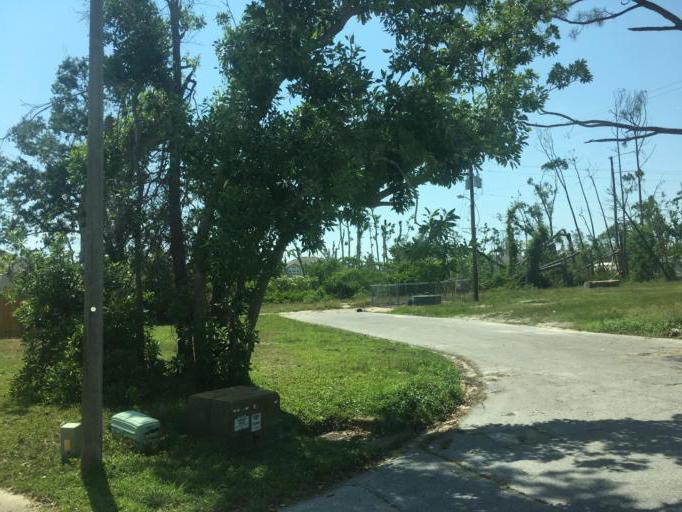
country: US
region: Florida
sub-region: Bay County
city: Lynn Haven
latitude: 30.2252
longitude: -85.6570
